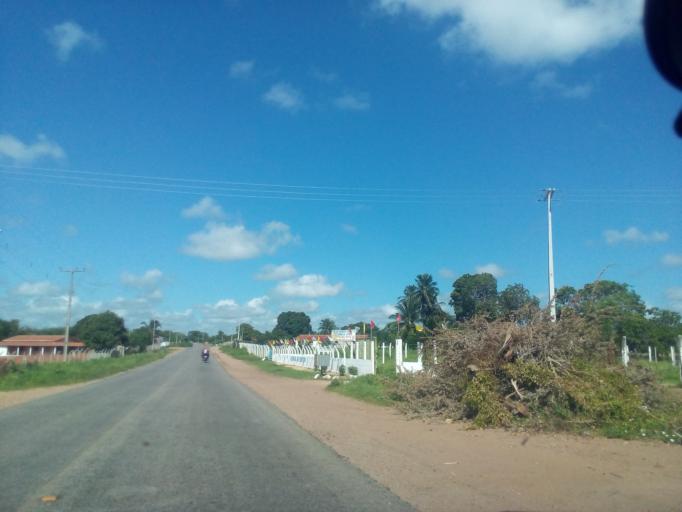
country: BR
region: Rio Grande do Norte
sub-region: Sao Paulo Do Potengi
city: Sao Paulo do Potengi
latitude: -5.9139
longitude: -35.7066
